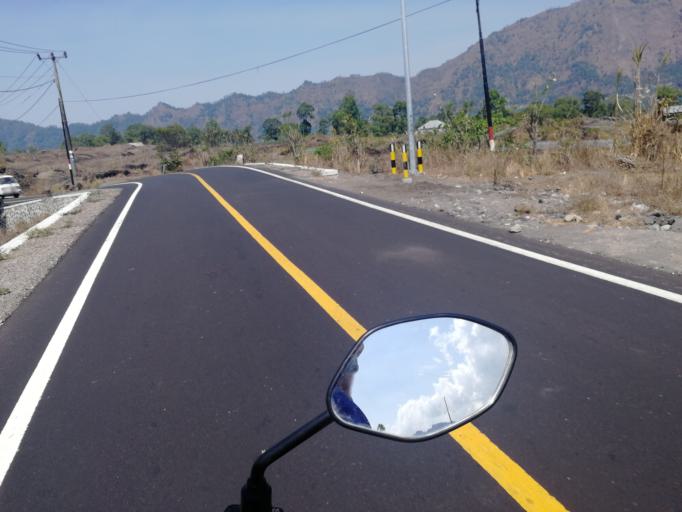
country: ID
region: Bali
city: Banjar Kedisan
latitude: -8.2573
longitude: 115.3938
